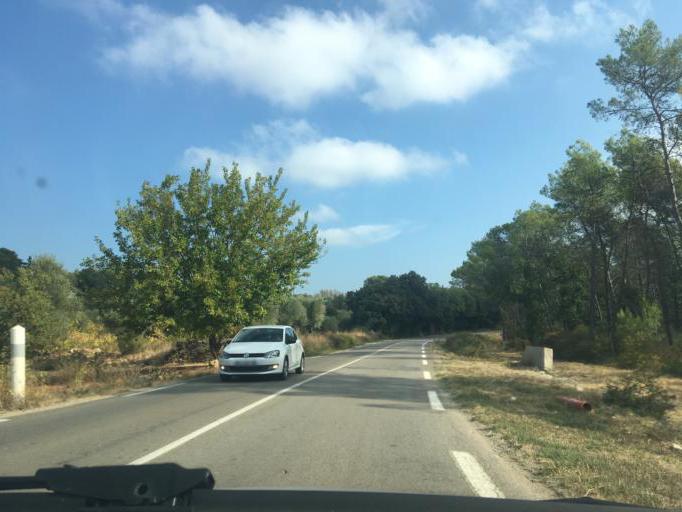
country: FR
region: Provence-Alpes-Cote d'Azur
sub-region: Departement du Var
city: Flayosc
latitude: 43.5065
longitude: 6.4209
